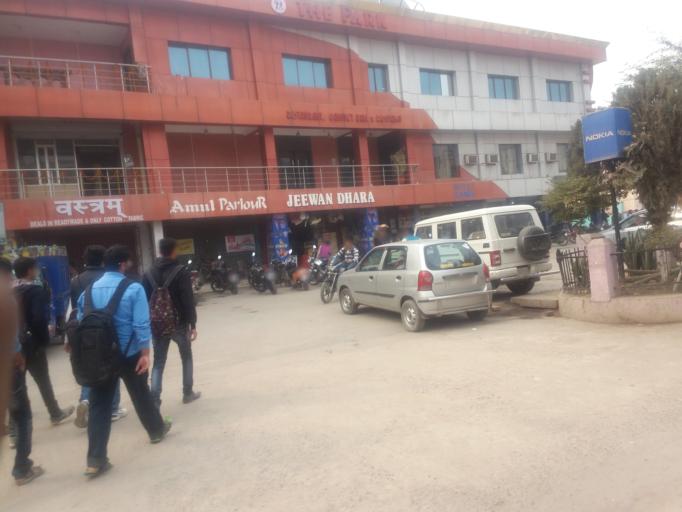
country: IN
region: Bihar
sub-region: Muzaffarpur
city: Muzaffarpur
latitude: 26.1112
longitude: 85.3962
